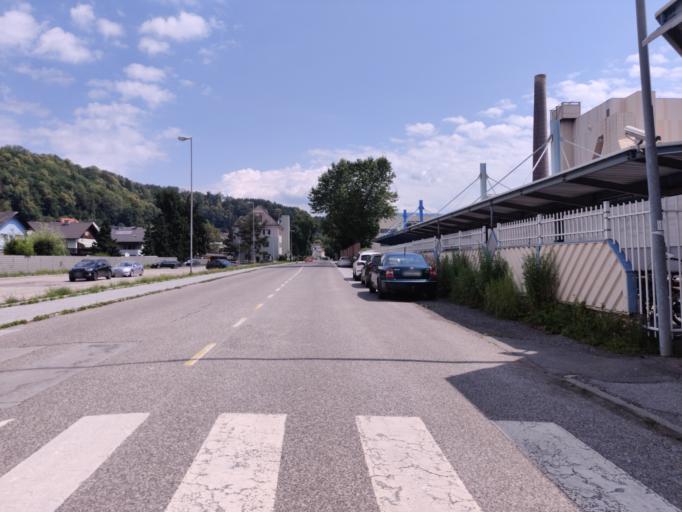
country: AT
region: Styria
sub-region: Politischer Bezirk Graz-Umgebung
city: Gratkorn
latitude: 47.1340
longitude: 15.3306
